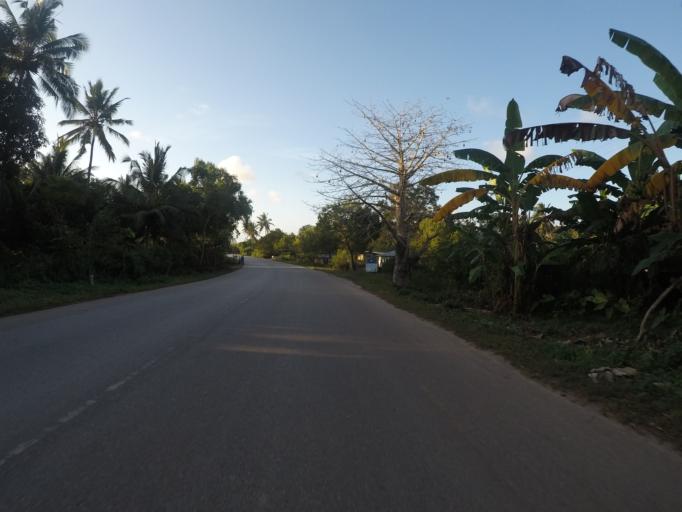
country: TZ
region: Zanzibar North
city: Kijini
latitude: -5.8249
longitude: 39.2918
